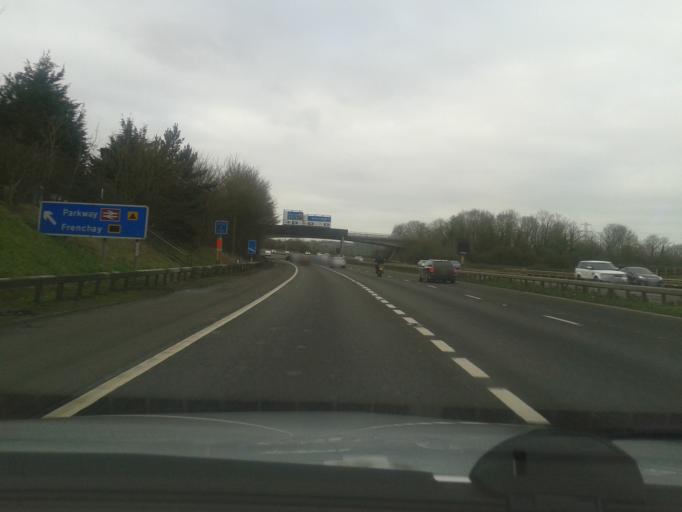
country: GB
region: England
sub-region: South Gloucestershire
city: Stoke Gifford
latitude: 51.5111
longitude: -2.5217
